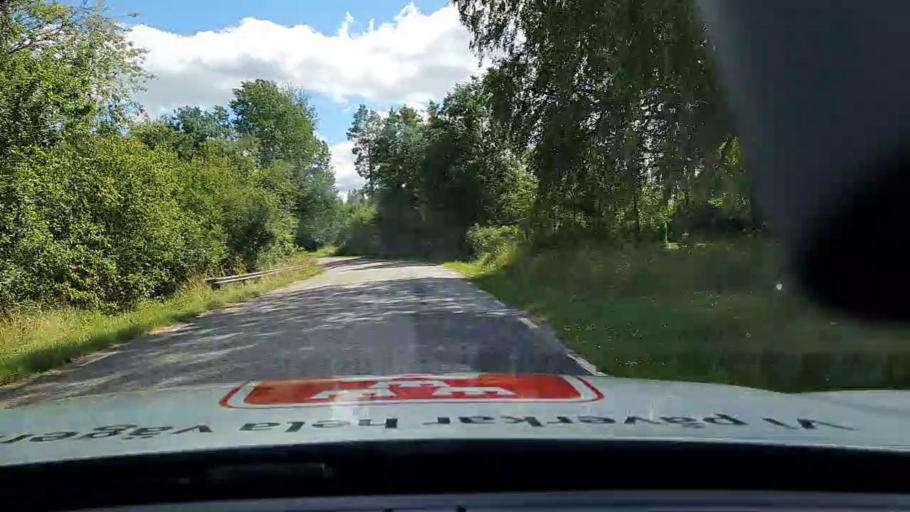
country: SE
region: Vaestra Goetaland
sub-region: Toreboda Kommun
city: Toereboda
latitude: 58.5713
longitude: 14.1275
